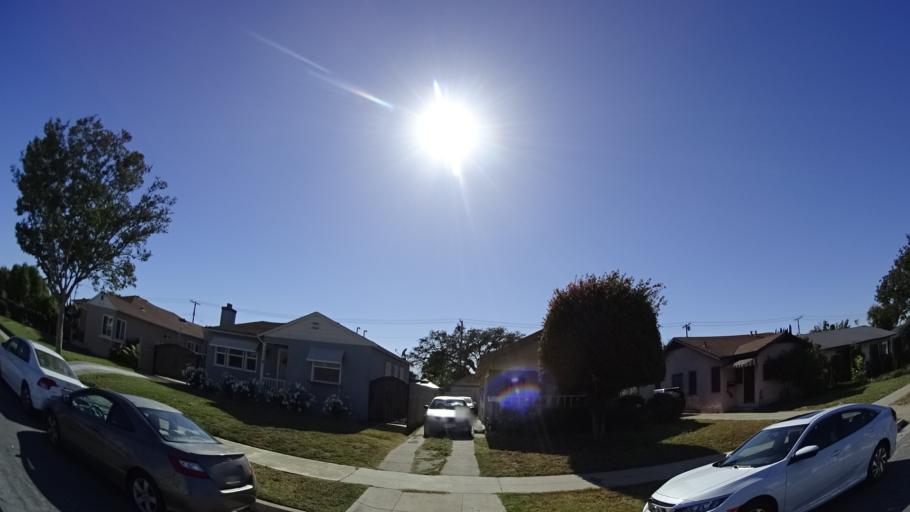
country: US
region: California
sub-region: Los Angeles County
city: Monterey Park
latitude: 34.0754
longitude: -118.1431
